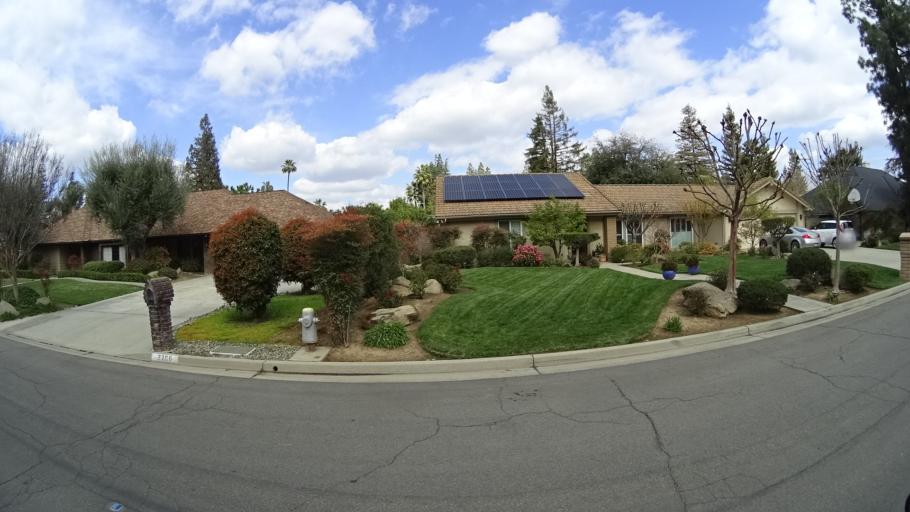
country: US
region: California
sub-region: Fresno County
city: Fresno
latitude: 36.8291
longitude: -119.8423
